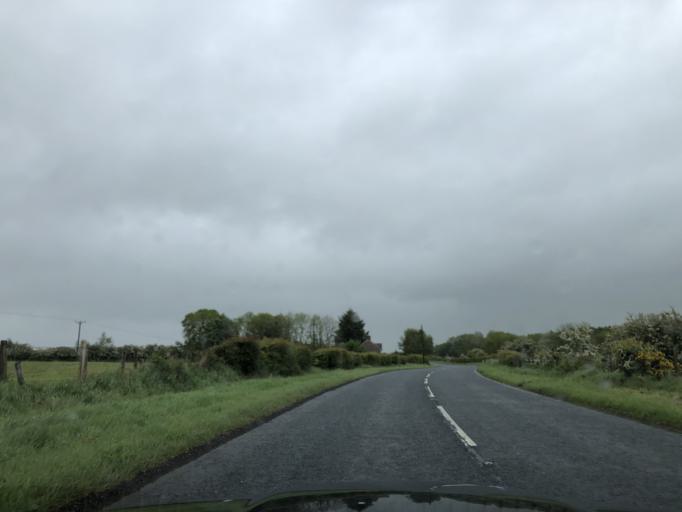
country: GB
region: Northern Ireland
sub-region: Moyle District
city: Ballycastle
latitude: 55.1810
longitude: -6.3236
